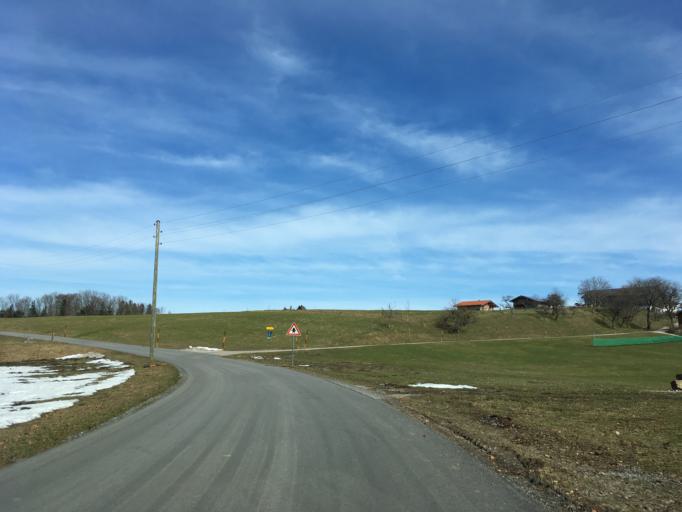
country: DE
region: Bavaria
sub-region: Upper Bavaria
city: Aschau im Chiemgau
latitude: 47.7990
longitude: 12.3420
